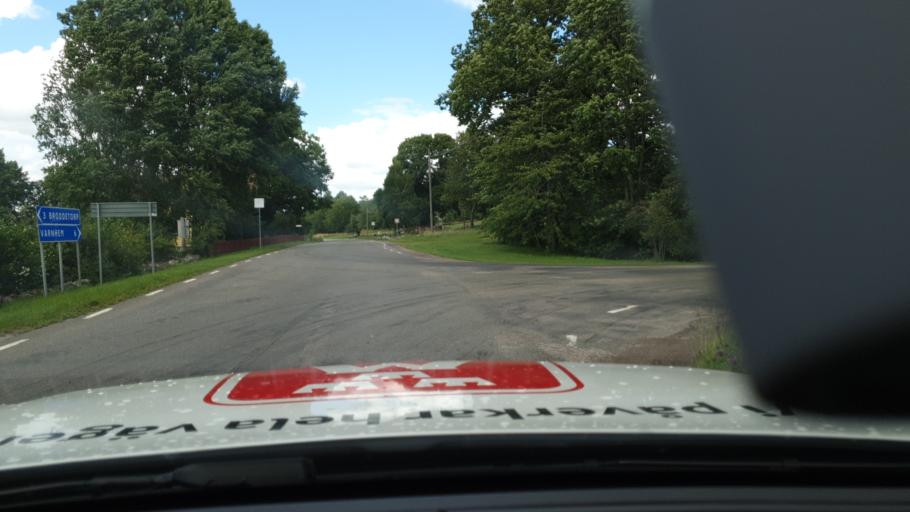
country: SE
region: Vaestra Goetaland
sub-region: Skara Kommun
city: Axvall
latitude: 58.3338
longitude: 13.6195
